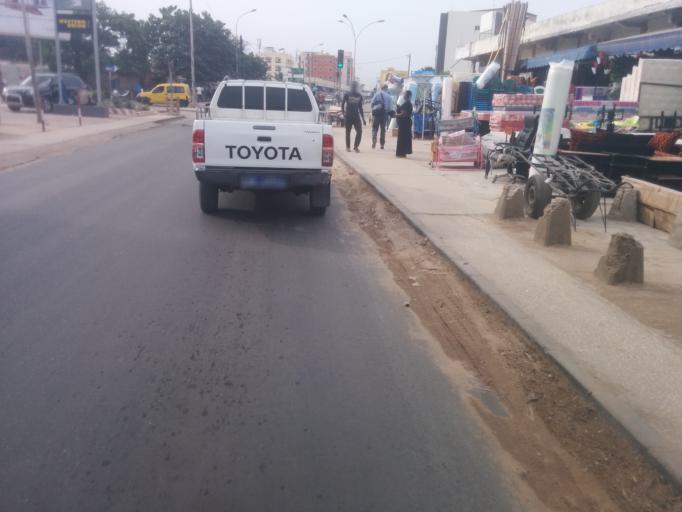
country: SN
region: Dakar
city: Grand Dakar
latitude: 14.7334
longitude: -17.4562
